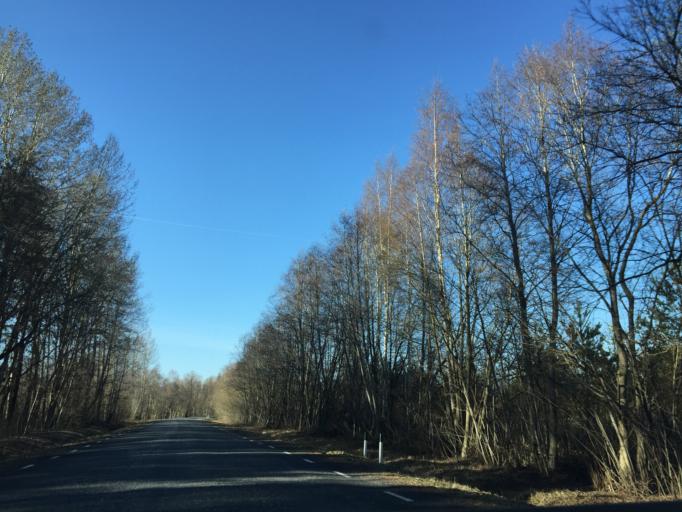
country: RU
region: Pskov
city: Gdov
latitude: 59.0312
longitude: 27.6879
